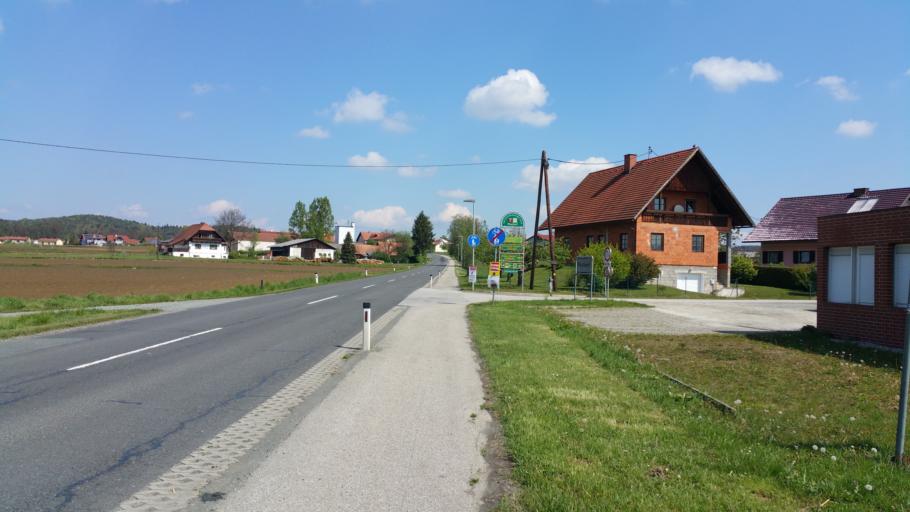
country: AT
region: Styria
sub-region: Politischer Bezirk Leibnitz
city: Gleinstatten
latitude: 46.7603
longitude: 15.3727
